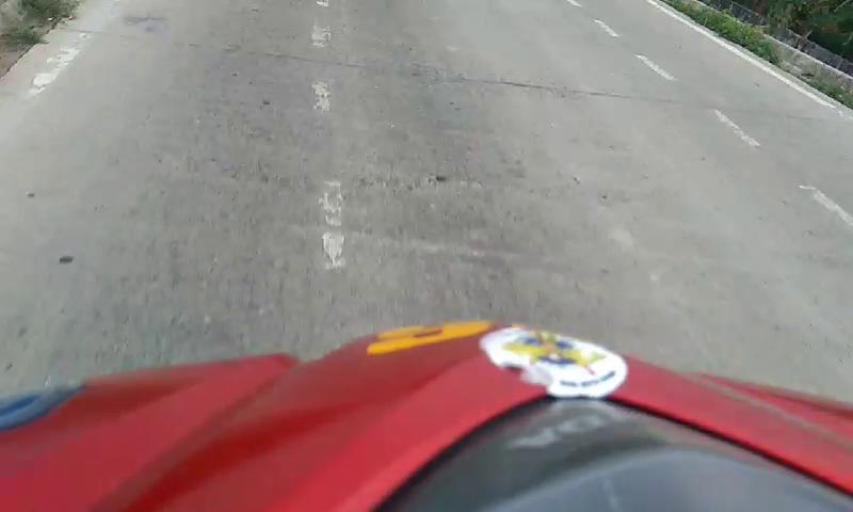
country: ID
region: West Java
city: Bekasi
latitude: -6.1437
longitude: 106.9701
